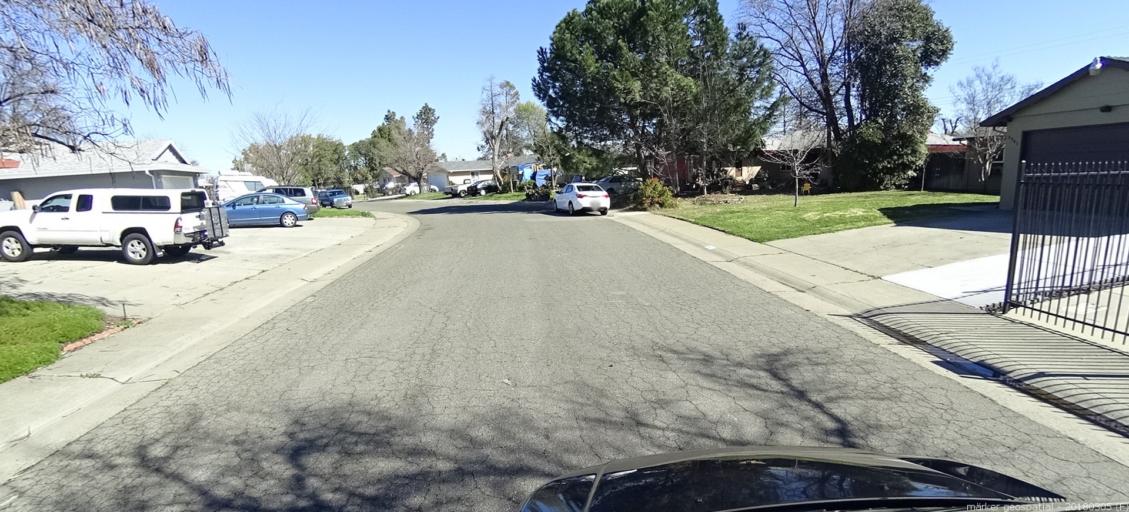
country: US
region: California
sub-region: Sacramento County
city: Florin
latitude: 38.5010
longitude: -121.4245
